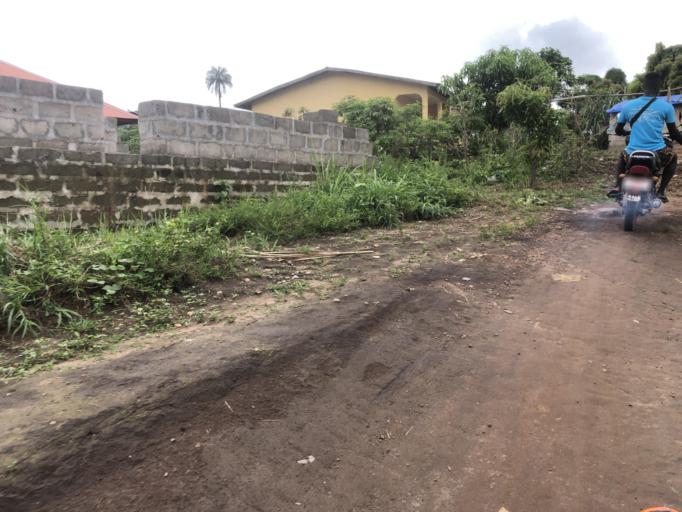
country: SL
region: Northern Province
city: Makeni
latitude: 8.9110
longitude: -12.0424
